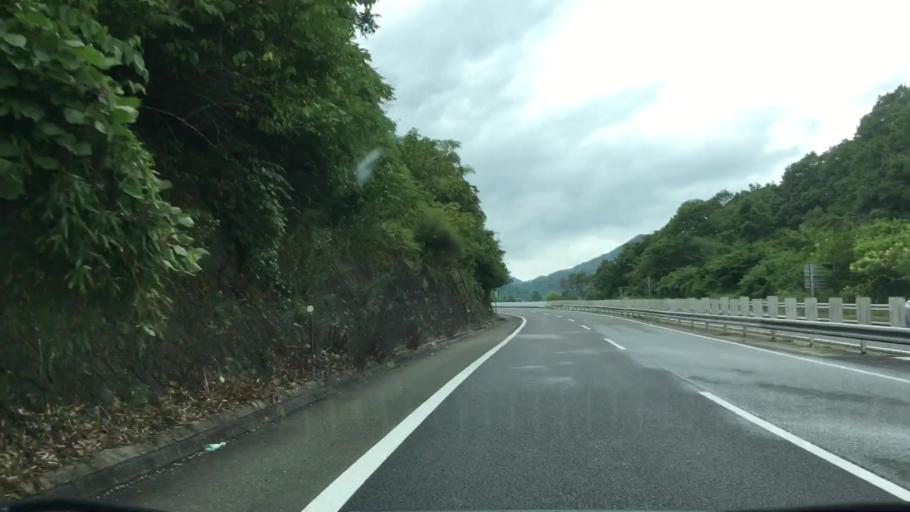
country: JP
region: Hiroshima
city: Shobara
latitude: 34.8952
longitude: 133.2417
